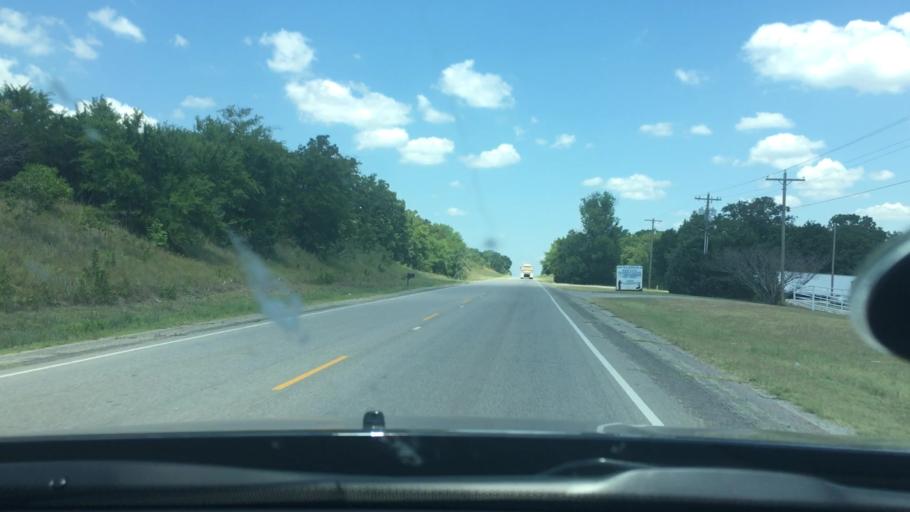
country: US
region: Oklahoma
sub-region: Marshall County
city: Oakland
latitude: 34.1504
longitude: -96.8128
